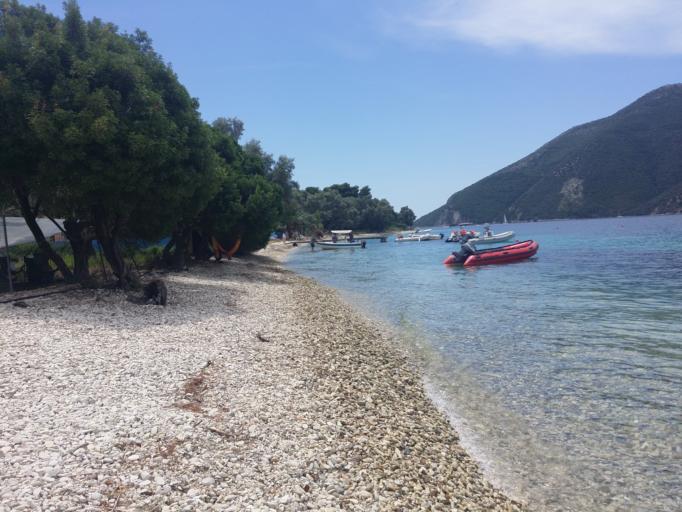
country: GR
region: Ionian Islands
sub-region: Lefkada
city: Nidri
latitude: 38.6469
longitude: 20.7385
